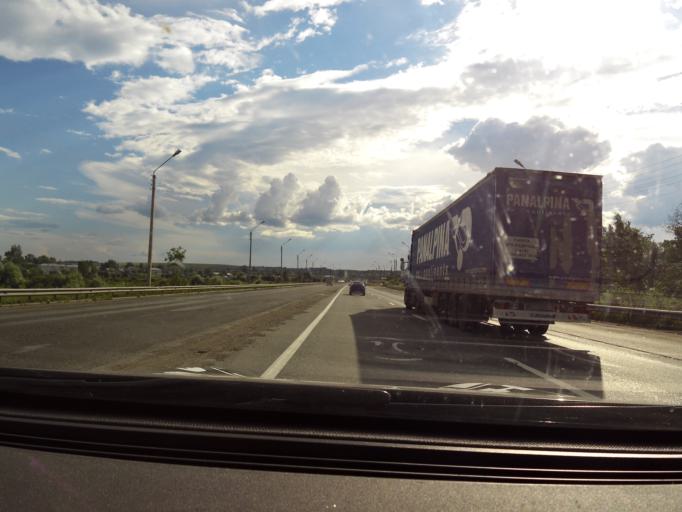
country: RU
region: Vladimir
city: Gorokhovets
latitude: 56.2022
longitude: 42.7159
